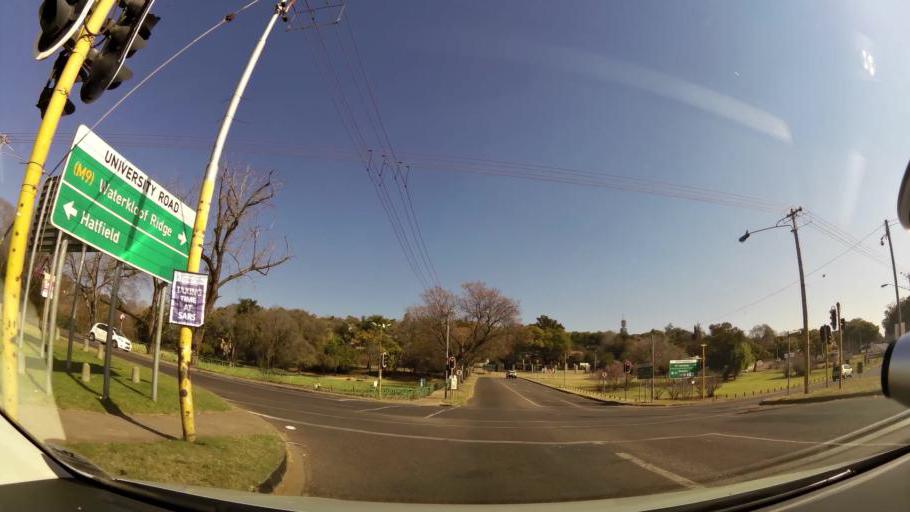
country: ZA
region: Gauteng
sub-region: City of Tshwane Metropolitan Municipality
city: Pretoria
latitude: -25.7608
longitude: 28.2199
